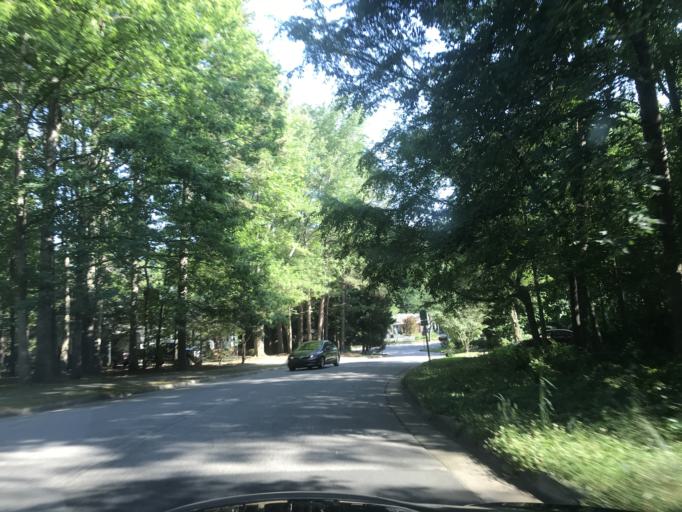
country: US
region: North Carolina
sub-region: Wake County
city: West Raleigh
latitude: 35.8639
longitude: -78.6169
